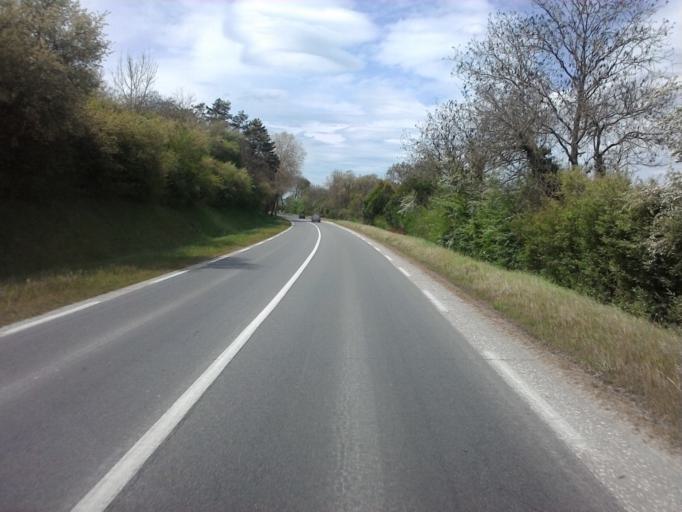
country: FR
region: Bourgogne
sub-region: Departement de l'Yonne
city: Champs-sur-Yonne
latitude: 47.7094
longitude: 3.6249
